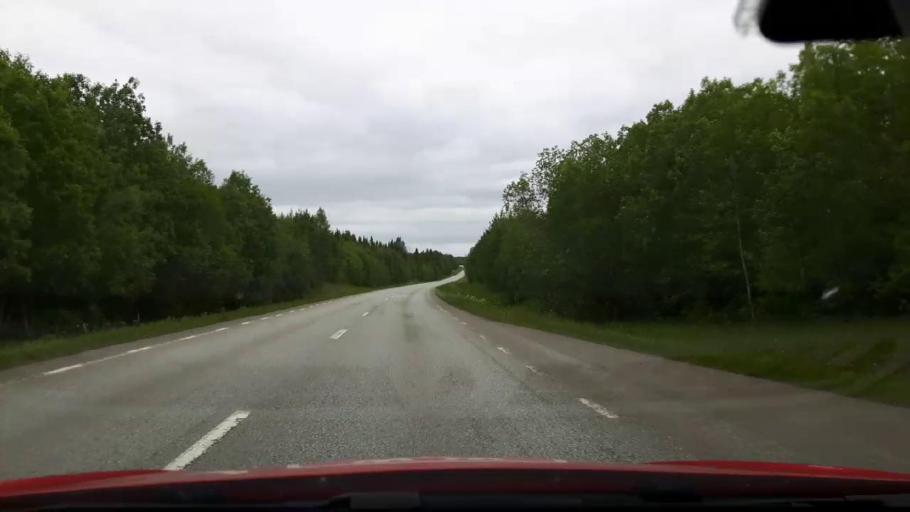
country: SE
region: Jaemtland
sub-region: OEstersunds Kommun
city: Lit
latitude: 63.5934
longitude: 14.6449
